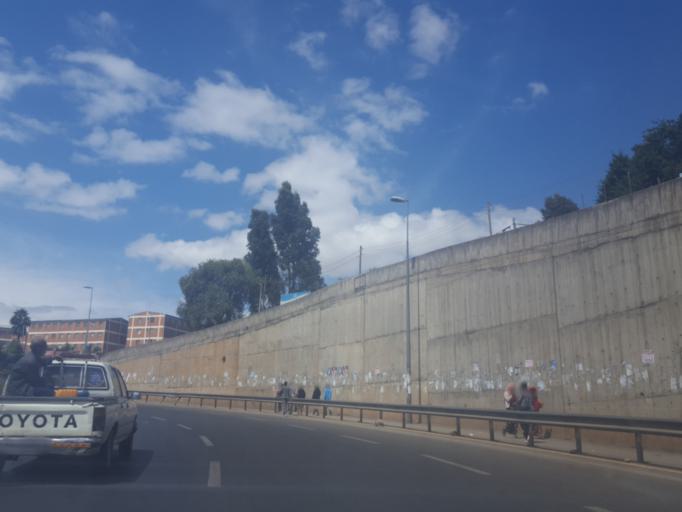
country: ET
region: Adis Abeba
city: Addis Ababa
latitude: 9.0631
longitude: 38.7346
